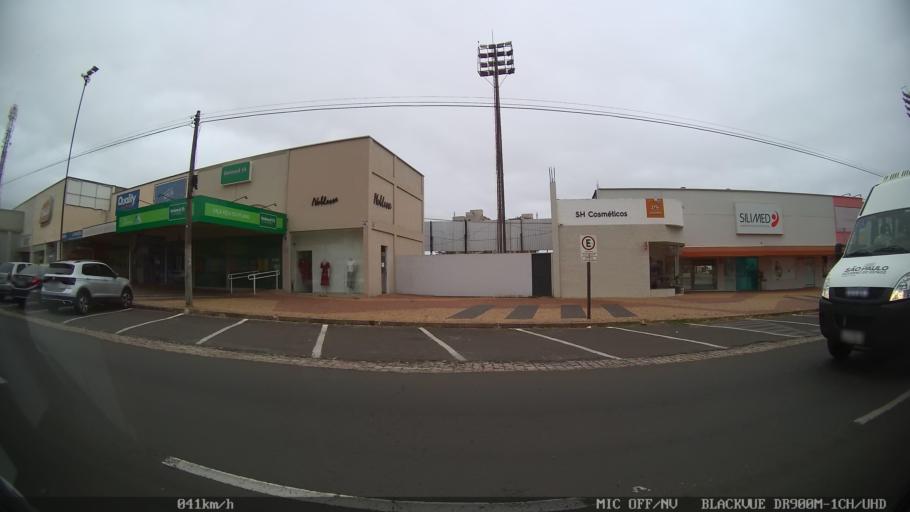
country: BR
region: Sao Paulo
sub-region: Sao Jose Do Rio Preto
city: Sao Jose do Rio Preto
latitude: -20.8350
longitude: -49.4003
